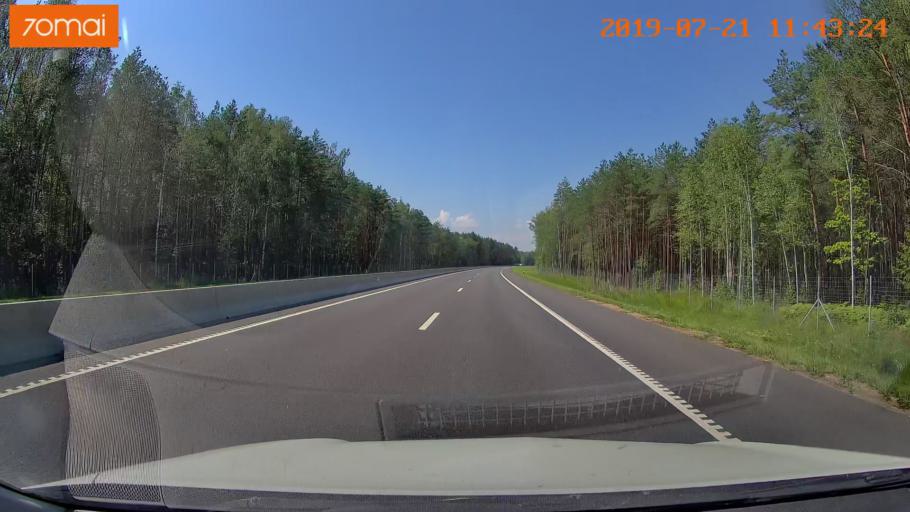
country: BY
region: Grodnenskaya
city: Lyubcha
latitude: 53.9216
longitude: 26.1164
